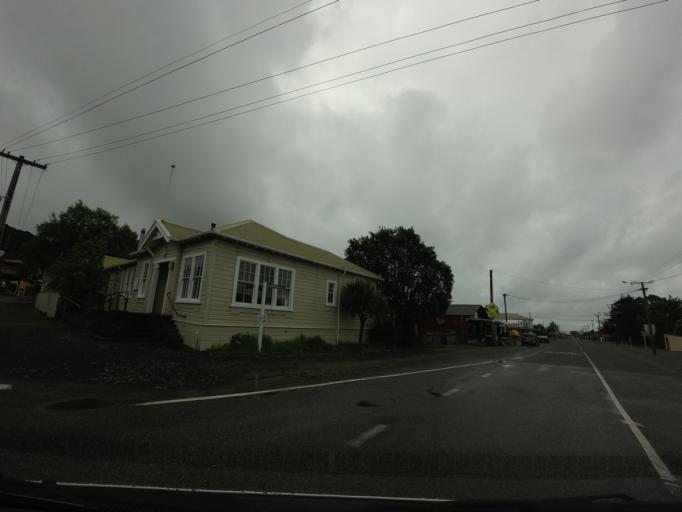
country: NZ
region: West Coast
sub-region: Westland District
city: Hokitika
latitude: -42.8993
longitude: 170.8174
